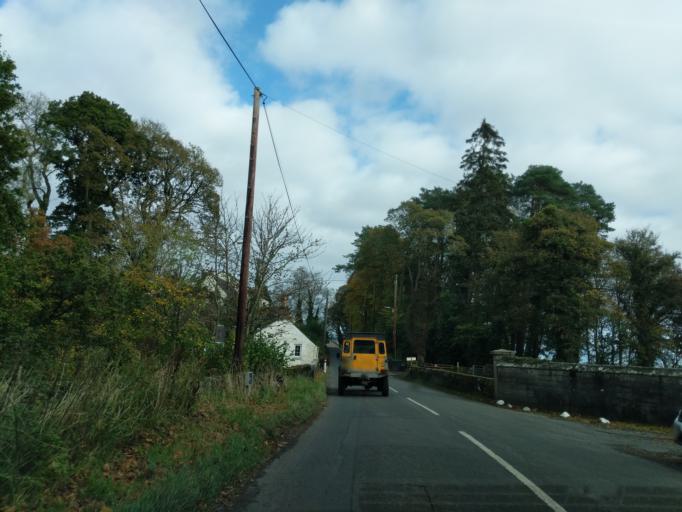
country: GB
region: Scotland
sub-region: Dumfries and Galloway
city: Thornhill
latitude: 55.2296
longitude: -3.8255
